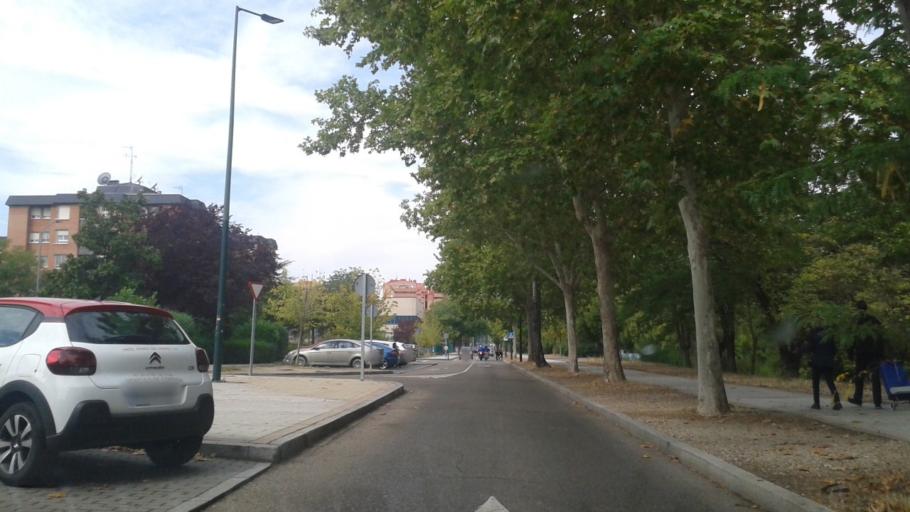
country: ES
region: Castille and Leon
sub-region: Provincia de Valladolid
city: Valladolid
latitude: 41.6600
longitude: -4.7353
